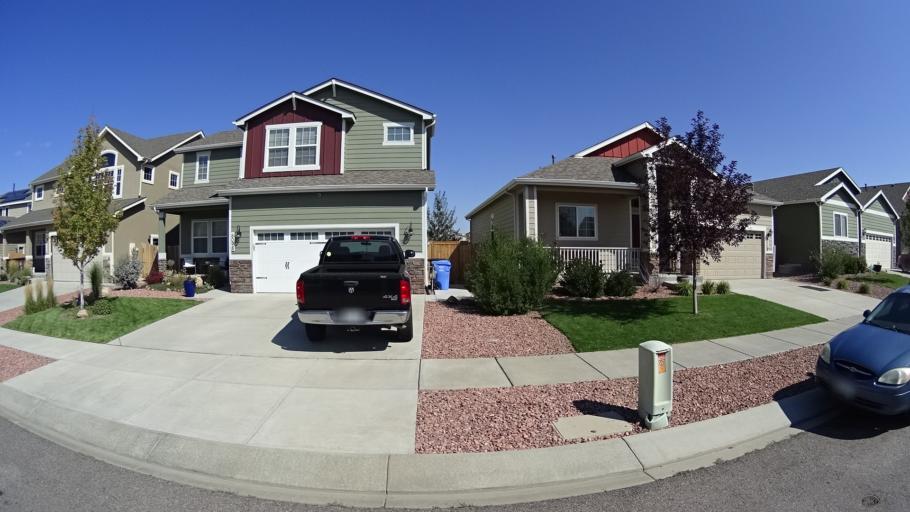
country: US
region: Colorado
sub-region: El Paso County
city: Cimarron Hills
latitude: 38.9296
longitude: -104.7115
